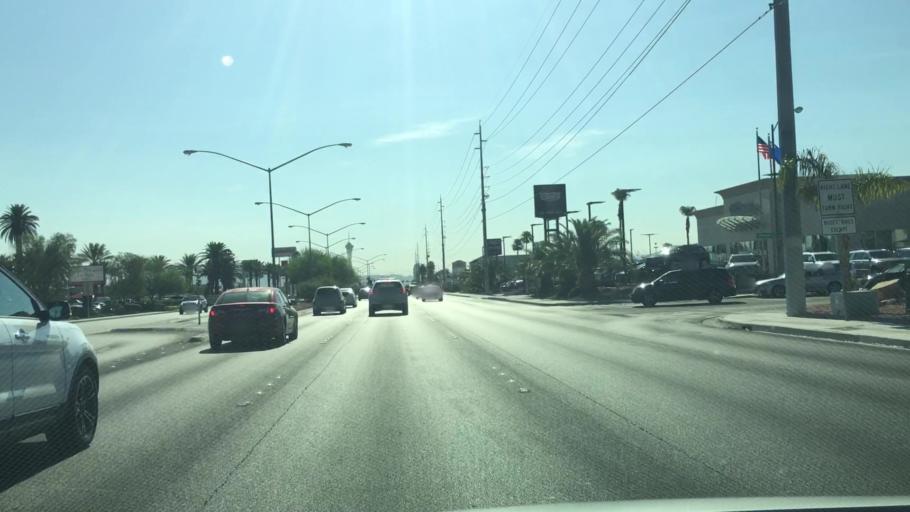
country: US
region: Nevada
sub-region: Clark County
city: Spring Valley
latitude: 36.1444
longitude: -115.2128
